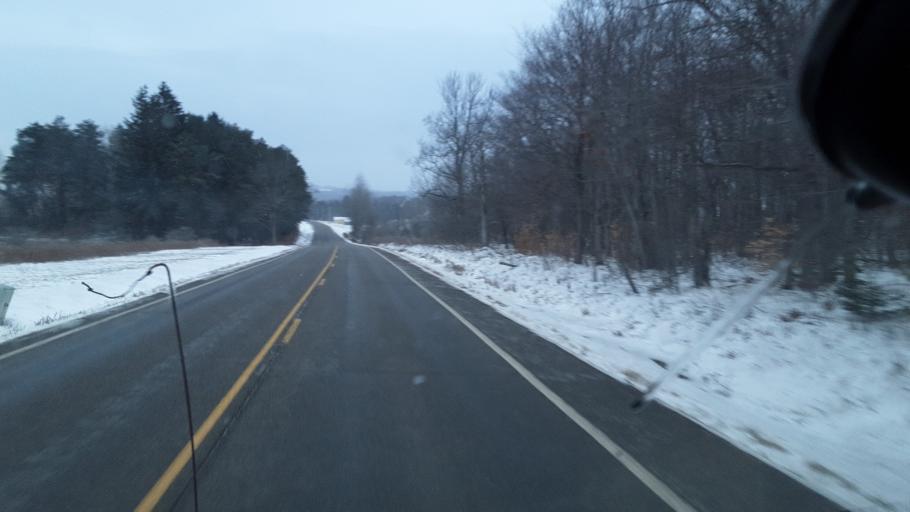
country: US
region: New York
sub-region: Allegany County
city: Andover
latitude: 42.0672
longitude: -77.8051
